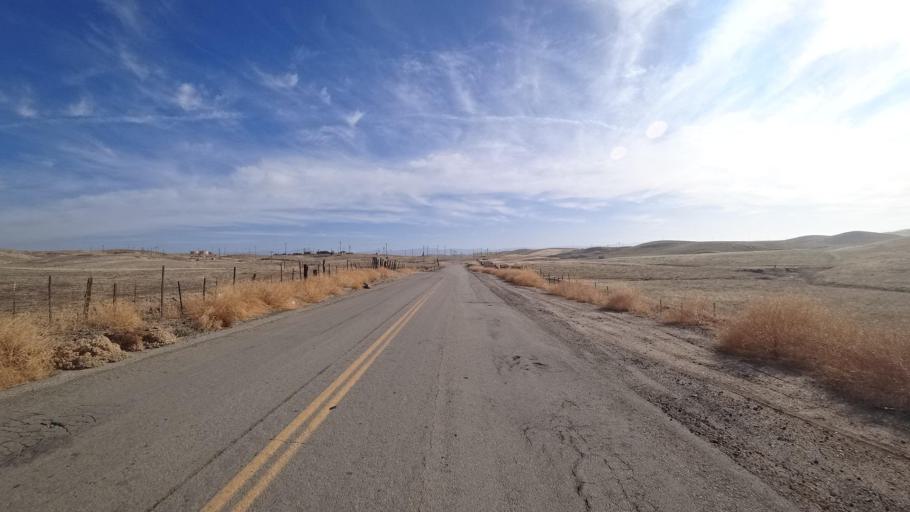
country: US
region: California
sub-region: Tulare County
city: Richgrove
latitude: 35.6266
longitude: -118.9920
